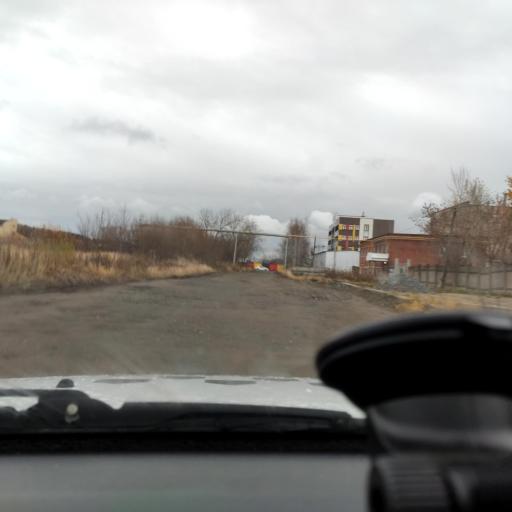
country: RU
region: Perm
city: Kondratovo
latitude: 57.9451
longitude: 56.1424
